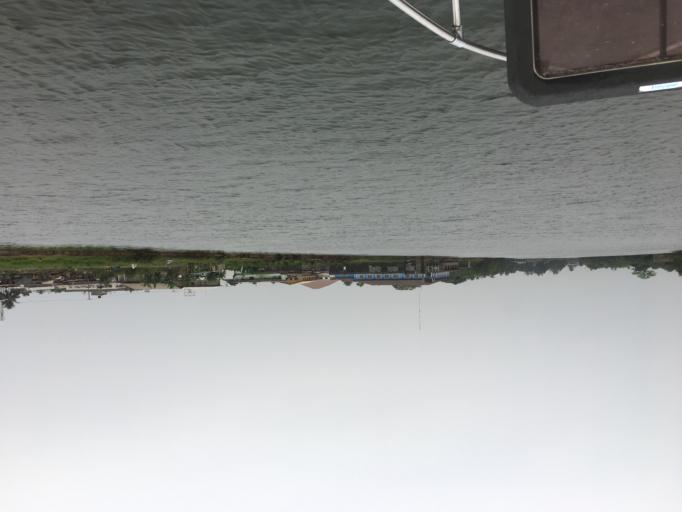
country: LR
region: Montserrado
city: Monrovia
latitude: 6.3841
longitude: -10.7803
